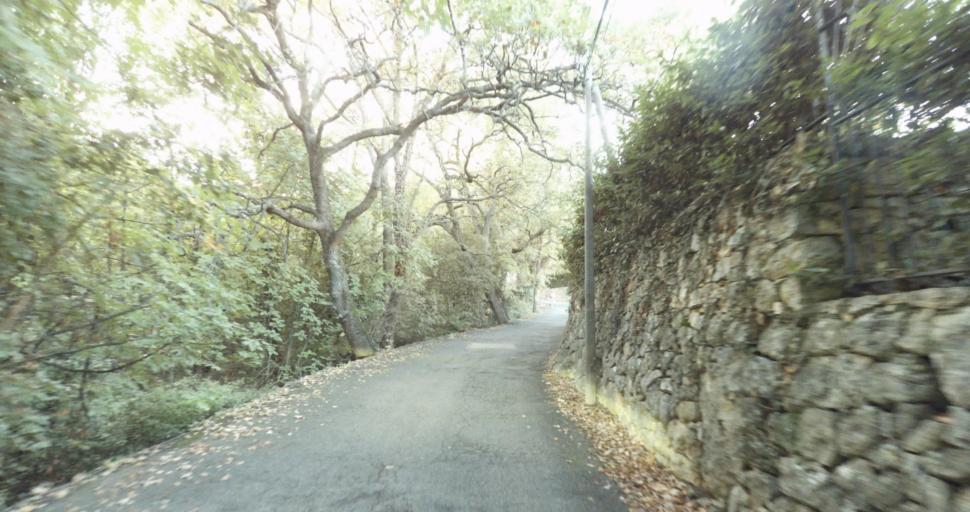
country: FR
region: Provence-Alpes-Cote d'Azur
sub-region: Departement des Alpes-Maritimes
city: Vence
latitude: 43.7319
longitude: 7.0988
